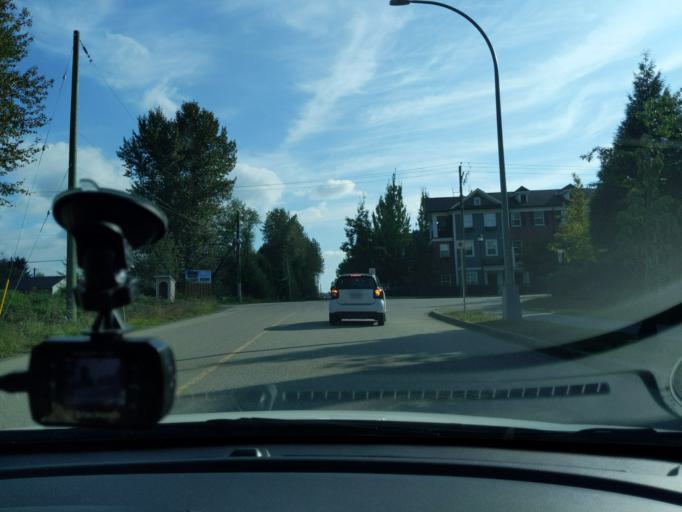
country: CA
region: British Columbia
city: Pitt Meadows
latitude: 49.2031
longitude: -122.6783
